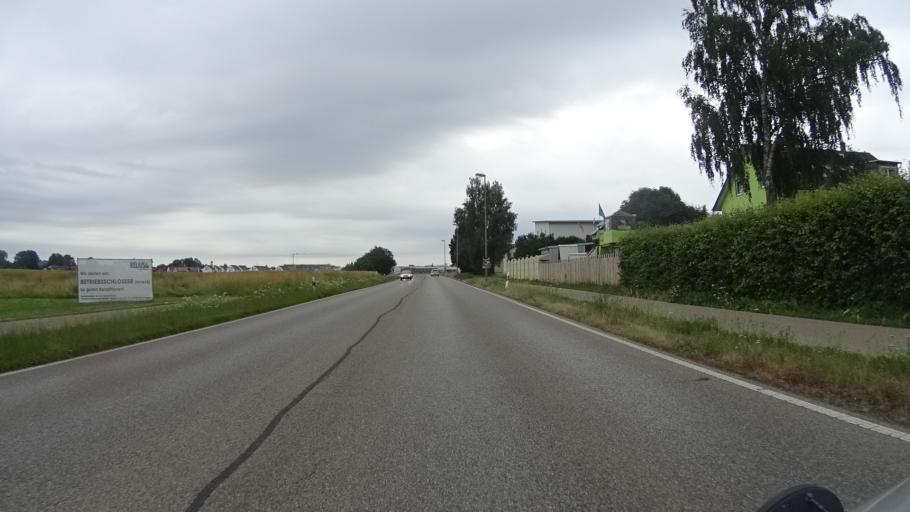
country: DE
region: Bavaria
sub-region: Swabia
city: Heimertingen
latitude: 48.0114
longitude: 10.1653
